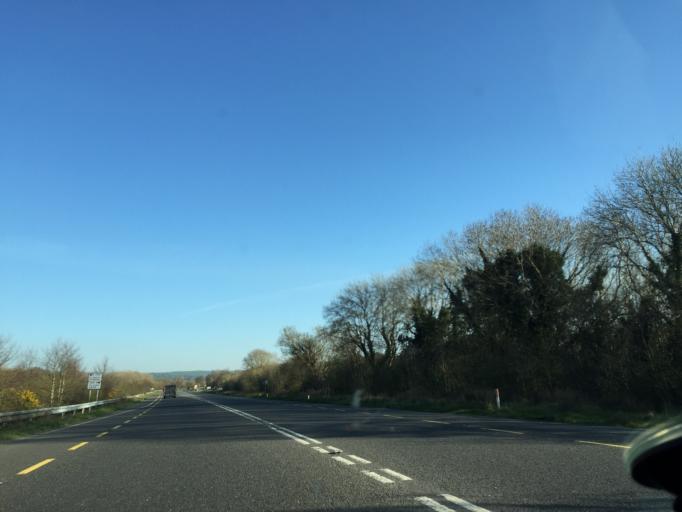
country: IE
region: Munster
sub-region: Ciarrai
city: Castleisland
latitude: 52.1954
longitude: -9.5690
